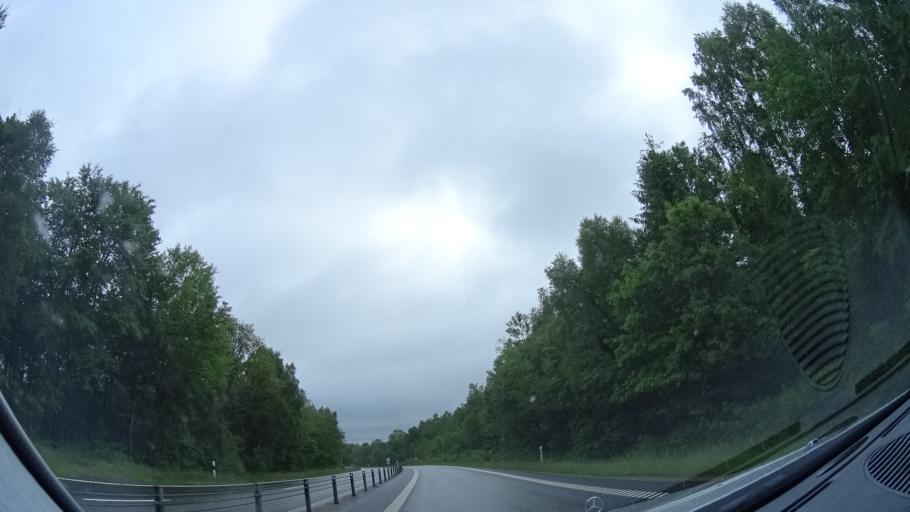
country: SE
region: Skane
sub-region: Hoors Kommun
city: Satofta
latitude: 55.9180
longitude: 13.5361
